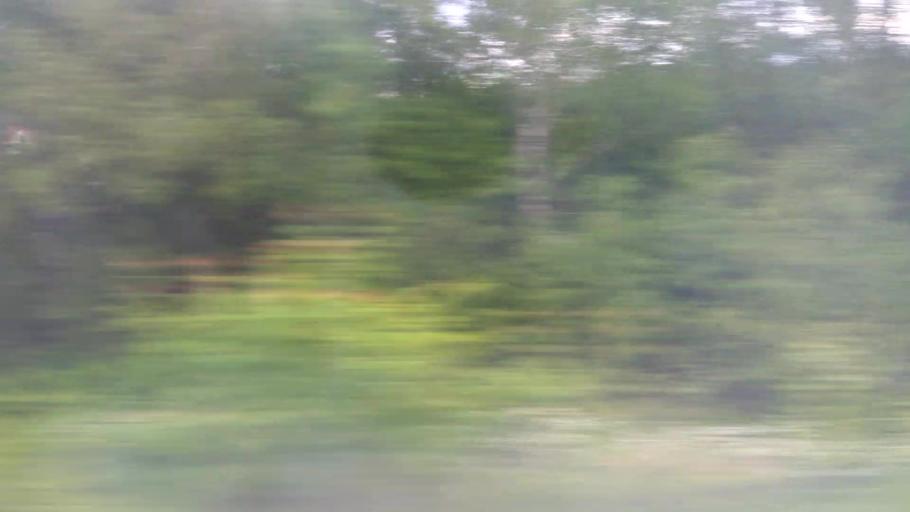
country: RU
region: Moskovskaya
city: Mikhnevo
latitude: 55.1864
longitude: 37.9297
